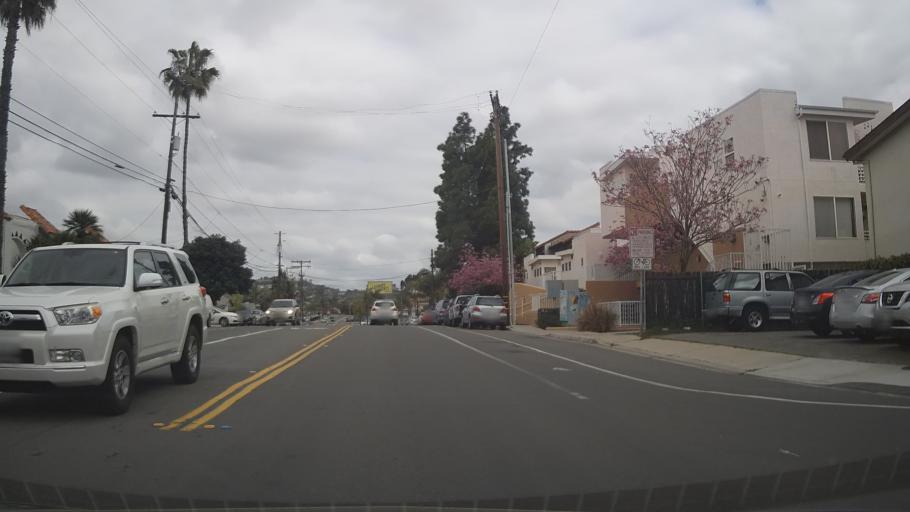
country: US
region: California
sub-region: San Diego County
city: La Mesa
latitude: 32.7660
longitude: -117.0470
